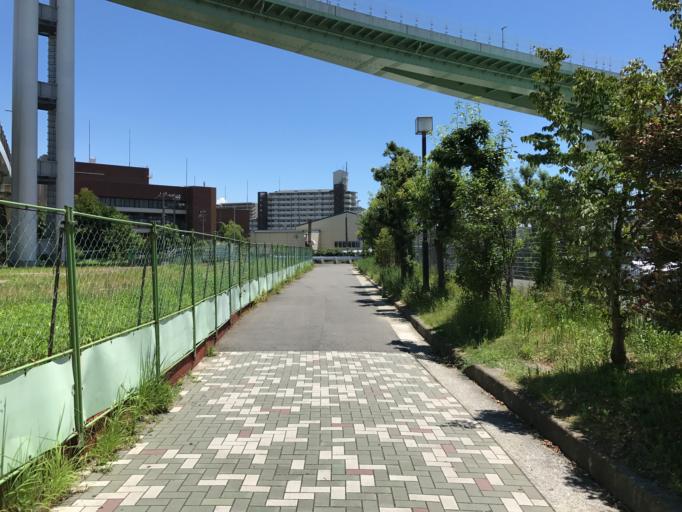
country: JP
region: Osaka
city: Osaka-shi
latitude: 34.6957
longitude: 135.4647
